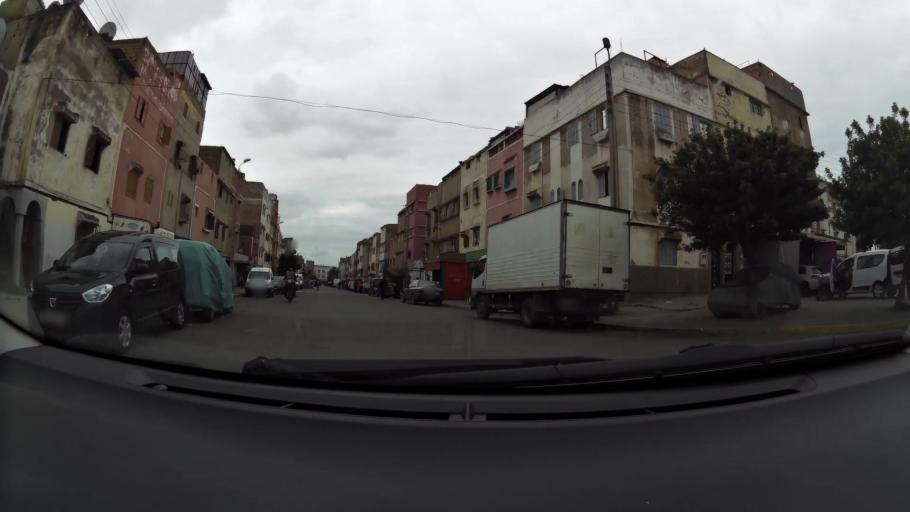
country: MA
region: Grand Casablanca
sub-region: Mediouna
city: Tit Mellil
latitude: 33.5642
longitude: -7.5416
